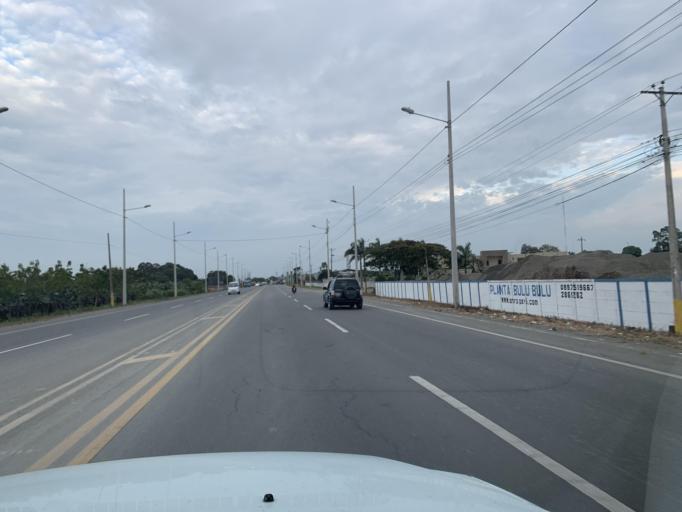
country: EC
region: Guayas
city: Yaguachi Nuevo
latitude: -2.2532
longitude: -79.6302
